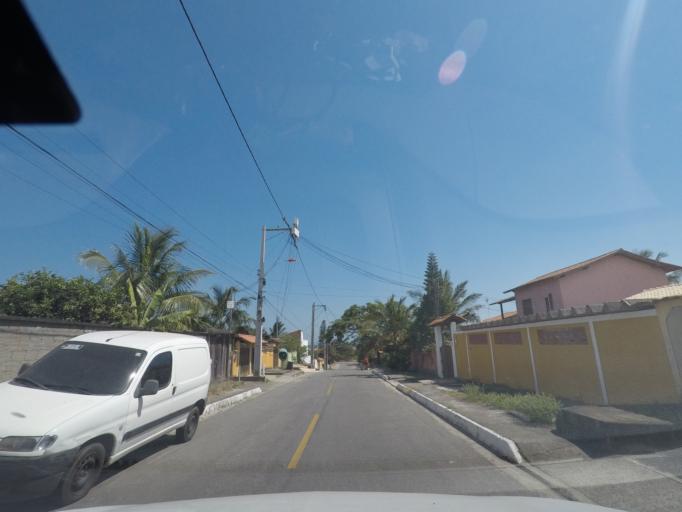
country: BR
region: Rio de Janeiro
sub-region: Marica
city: Marica
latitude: -22.9664
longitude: -42.9649
